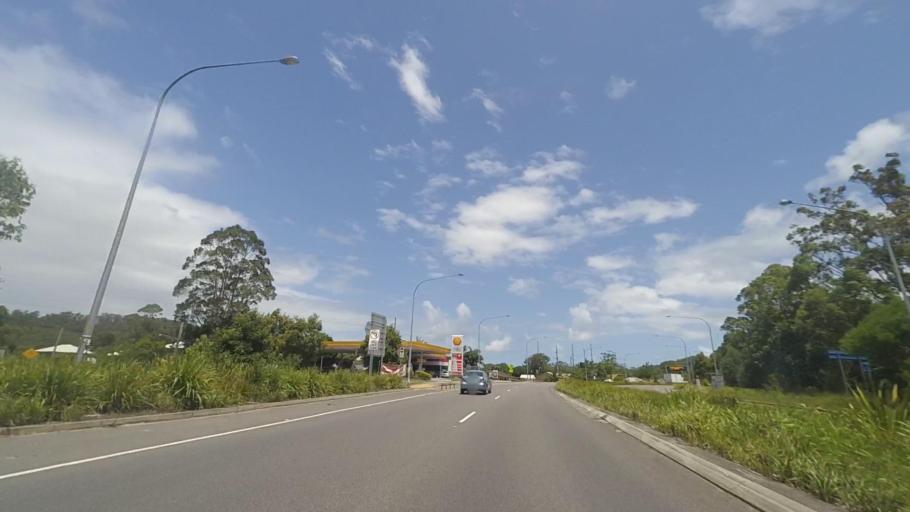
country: AU
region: New South Wales
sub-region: Gosford Shire
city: Lisarow
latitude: -33.3462
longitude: 151.3706
